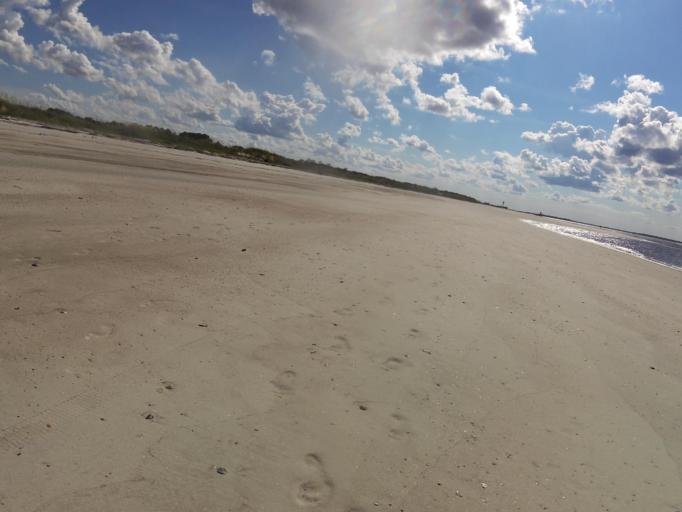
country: US
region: Florida
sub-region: Nassau County
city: Fernandina Beach
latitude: 30.7045
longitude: -81.4360
